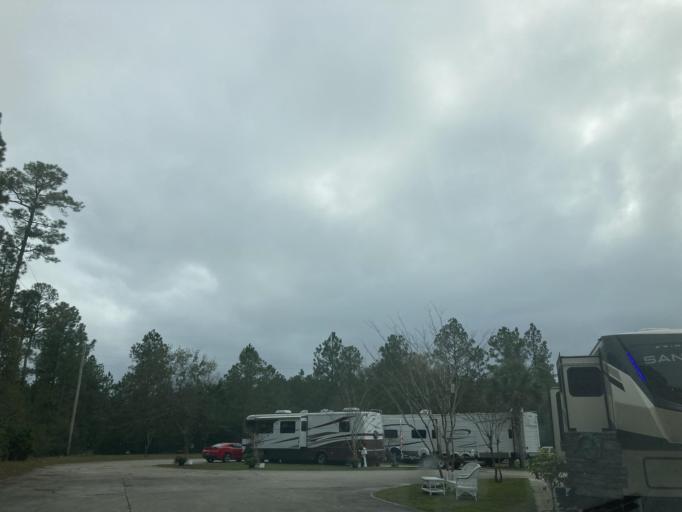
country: US
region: Mississippi
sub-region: Jackson County
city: Latimer
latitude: 30.5381
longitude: -88.9219
